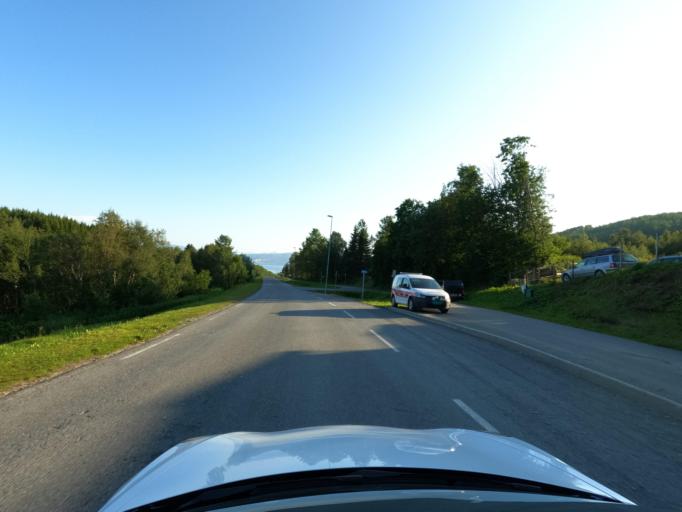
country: NO
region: Nordland
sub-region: Evenes
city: Randa
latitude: 68.4881
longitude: 16.8990
